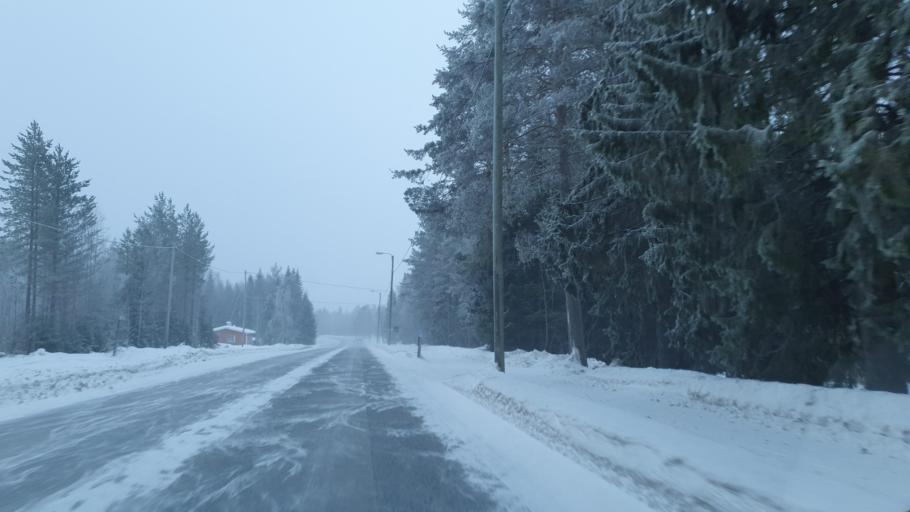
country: FI
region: Lapland
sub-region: Kemi-Tornio
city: Tornio
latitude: 66.0290
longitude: 24.0337
